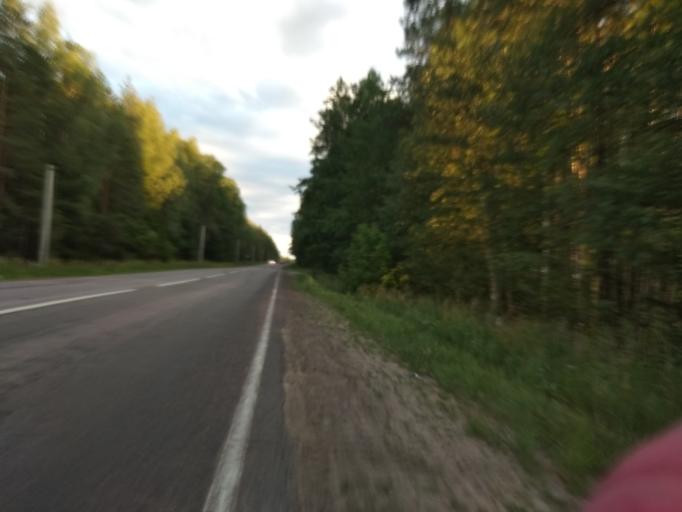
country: RU
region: Moskovskaya
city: Misheronskiy
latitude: 55.6166
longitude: 39.7240
